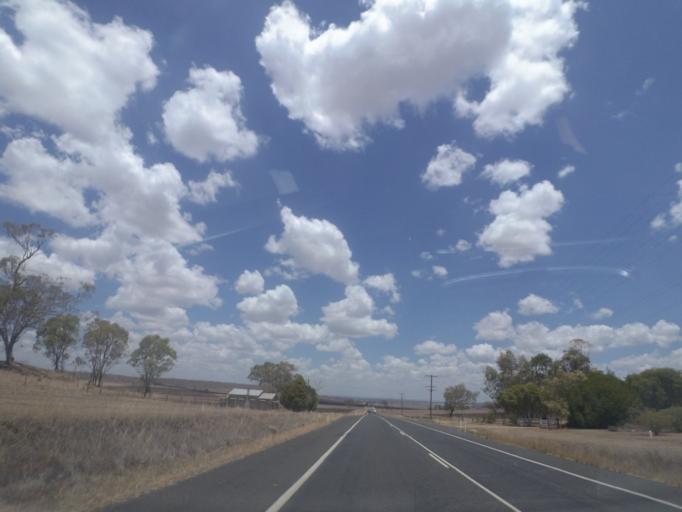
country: AU
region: Queensland
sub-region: Southern Downs
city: Warwick
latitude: -27.9936
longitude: 151.9968
